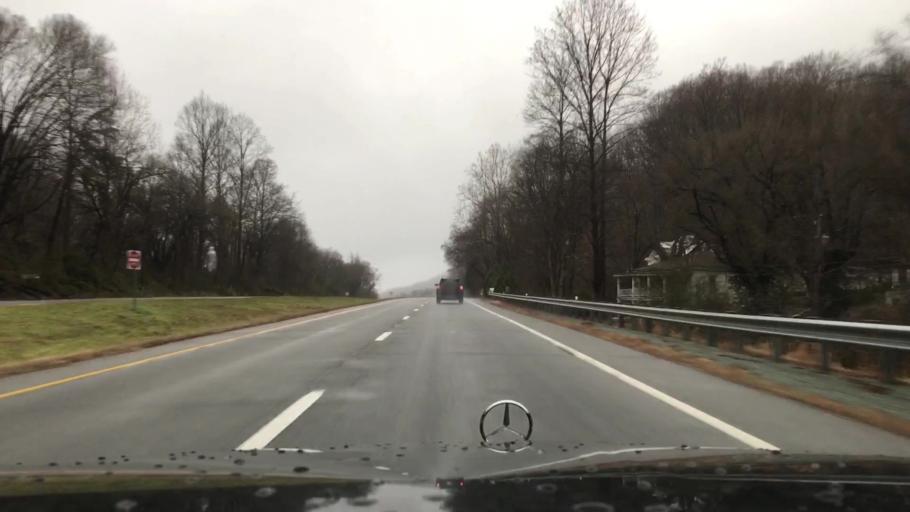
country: US
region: Virginia
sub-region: Nelson County
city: Nellysford
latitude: 37.8900
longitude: -78.7055
